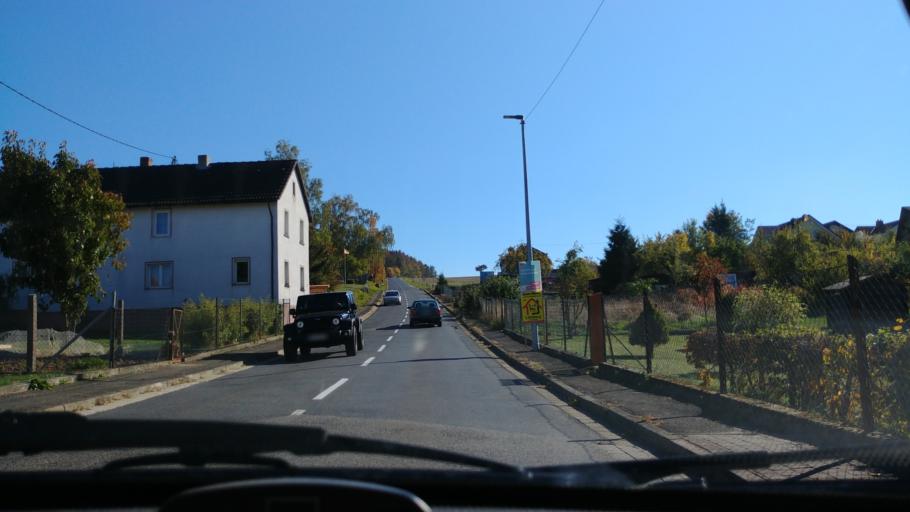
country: DE
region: Hesse
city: Burg Hohenstein
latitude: 50.2102
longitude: 8.0905
